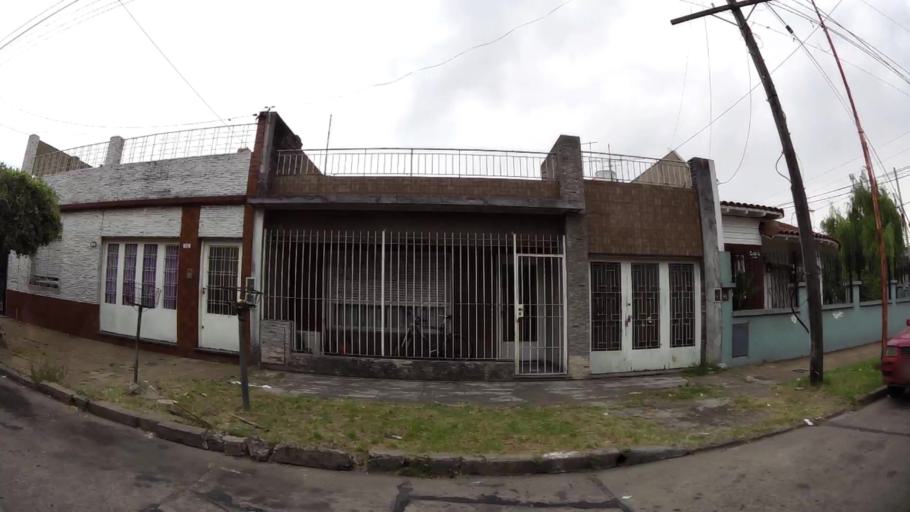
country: AR
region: Buenos Aires
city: San Justo
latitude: -34.6652
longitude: -58.5319
